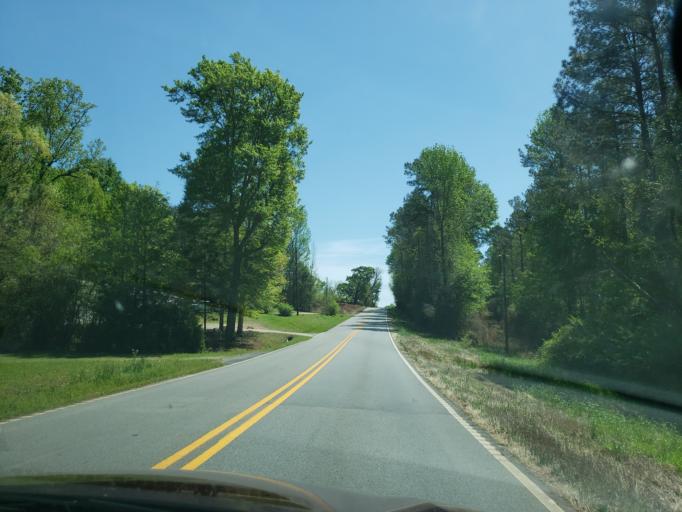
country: US
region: Alabama
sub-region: Tallapoosa County
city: Dadeville
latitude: 32.7019
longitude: -85.7478
